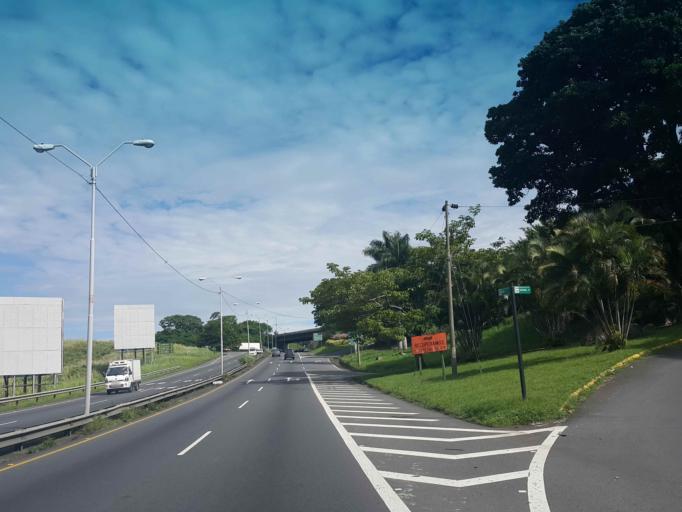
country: CR
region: San Jose
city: Colima
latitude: 9.9443
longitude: -84.1060
